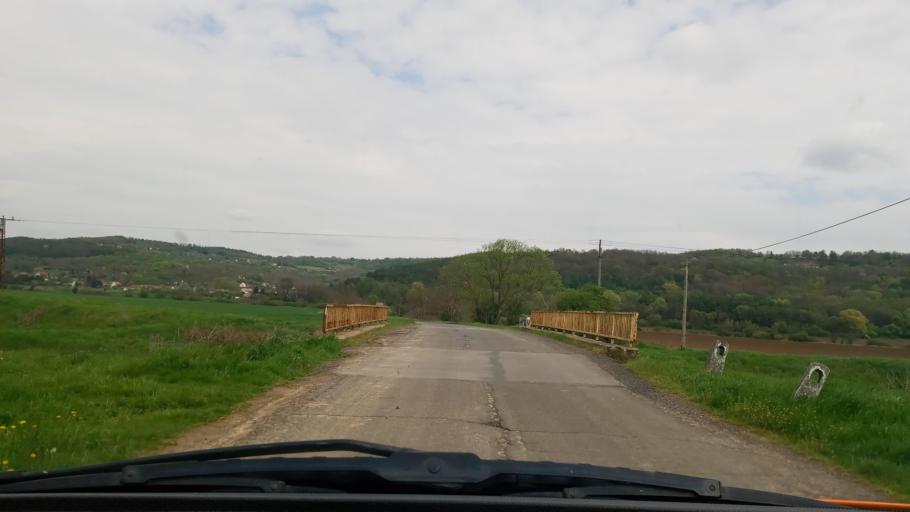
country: HU
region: Baranya
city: Sasd
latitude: 46.2592
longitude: 18.1150
